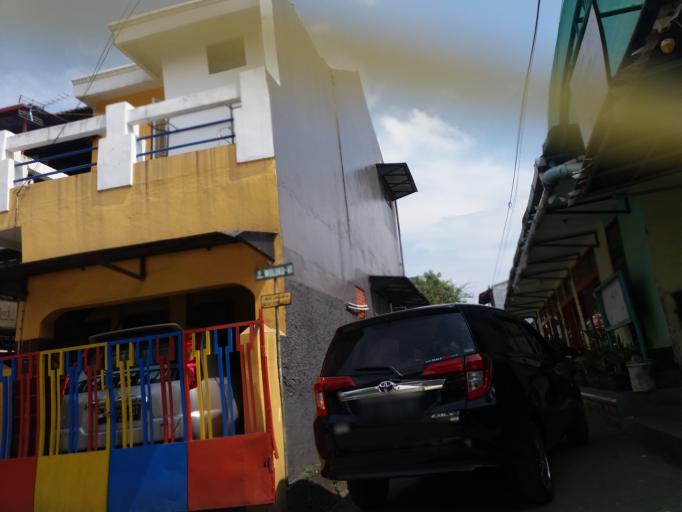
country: ID
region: West Java
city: Bandung
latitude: -6.9194
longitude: 107.6496
